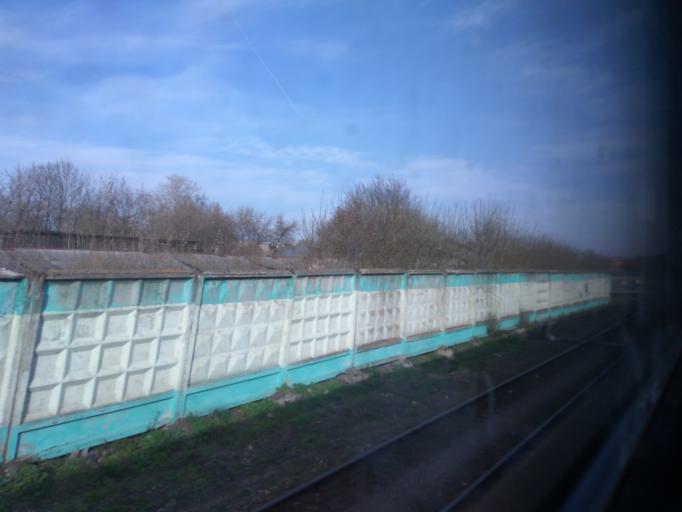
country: RU
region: Moskovskaya
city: Ramenskoye
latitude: 55.5557
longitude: 38.2531
